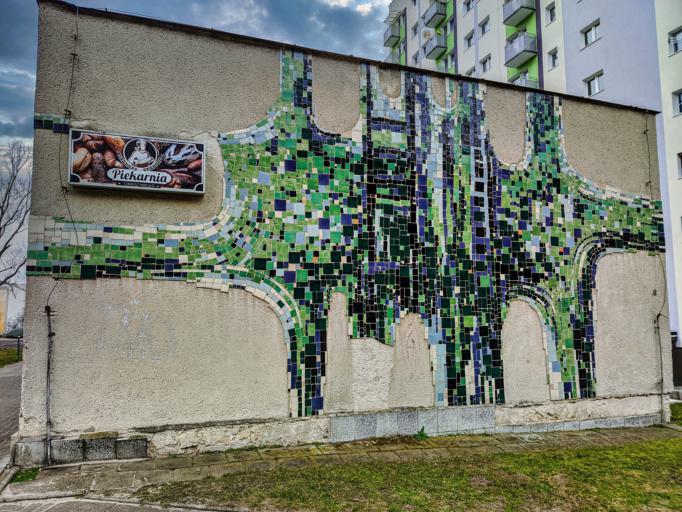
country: PL
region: Lubusz
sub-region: Zielona Gora
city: Zielona Gora
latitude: 51.9347
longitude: 15.4839
